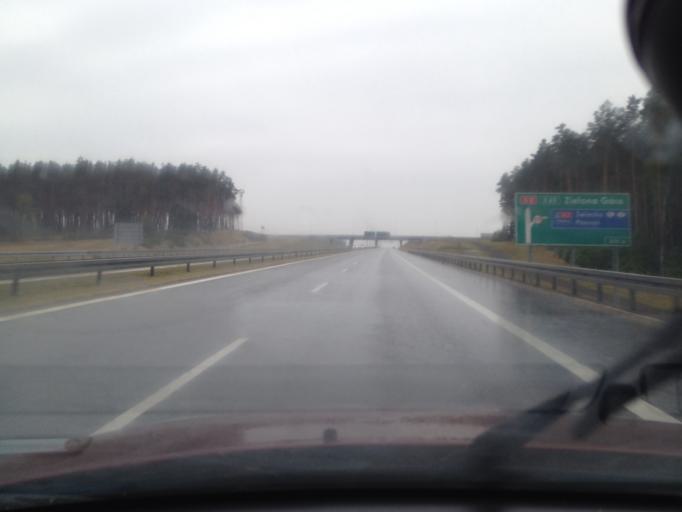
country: PL
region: Lubusz
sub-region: Powiat swiebodzinski
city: Swiebodzin
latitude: 52.3278
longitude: 15.5542
